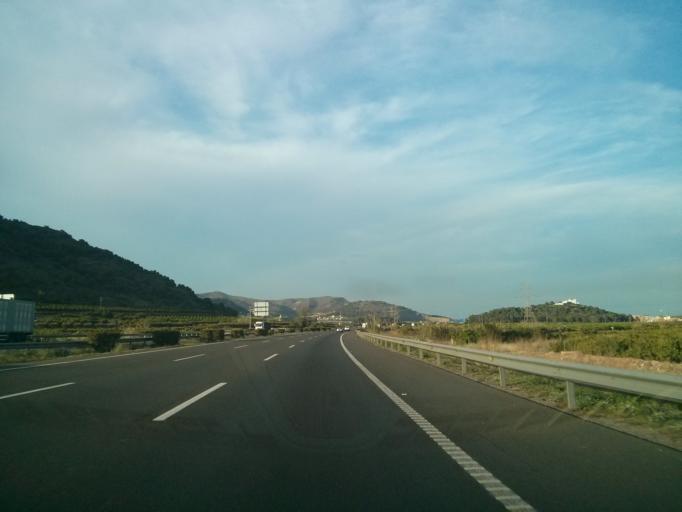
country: ES
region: Valencia
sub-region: Provincia de Valencia
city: Petres
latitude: 39.6807
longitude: -0.2982
